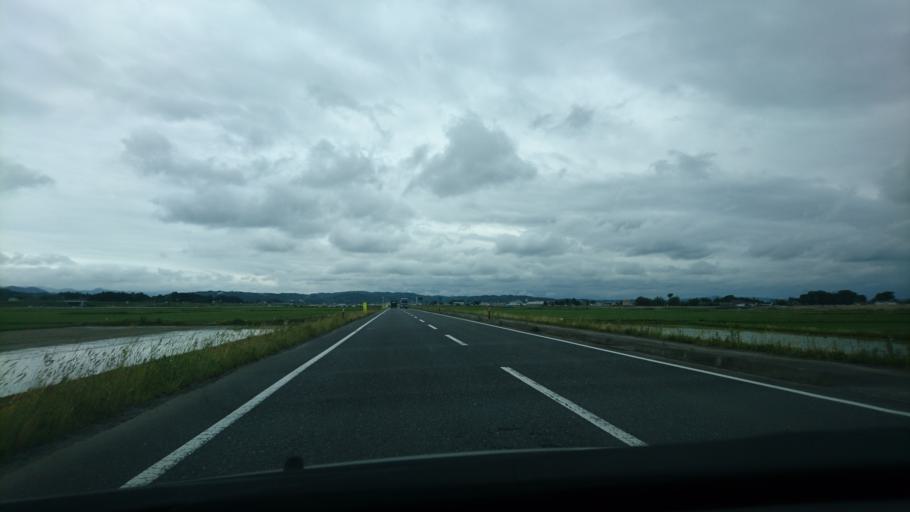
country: JP
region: Miyagi
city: Wakuya
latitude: 38.6832
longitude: 141.2610
